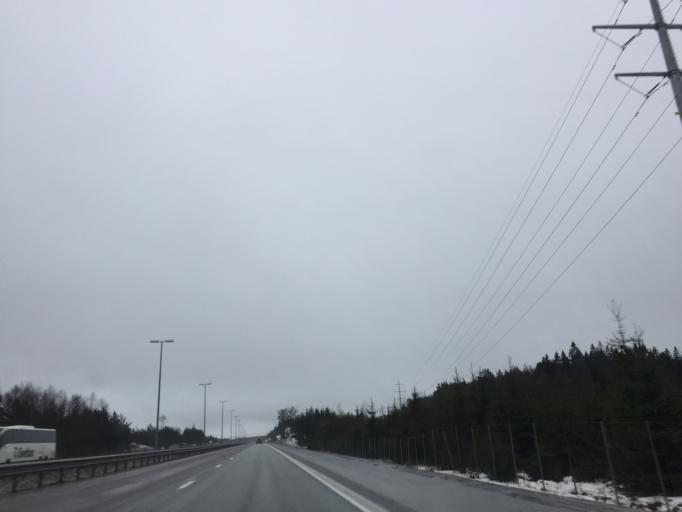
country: NO
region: Akershus
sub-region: Vestby
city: Vestby
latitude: 59.5529
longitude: 10.7221
